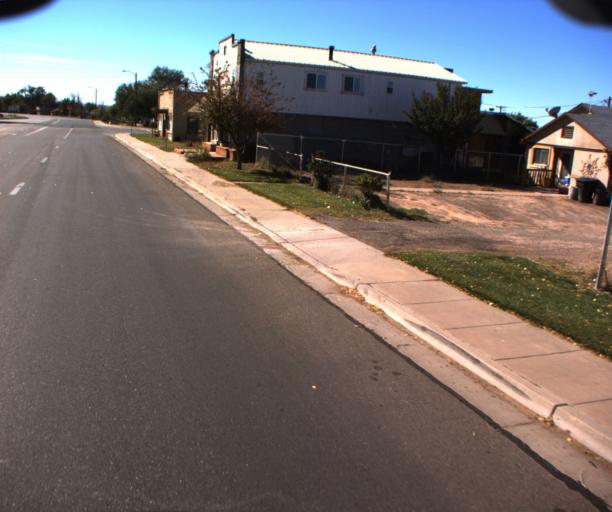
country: US
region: Arizona
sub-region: Coconino County
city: Fredonia
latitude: 36.9466
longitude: -112.5265
